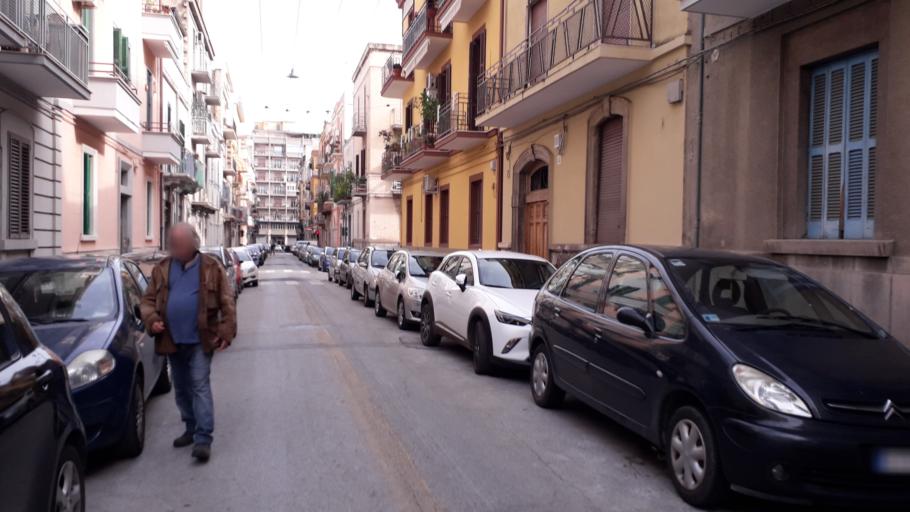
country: IT
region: Apulia
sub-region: Provincia di Bari
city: Bari
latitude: 41.1139
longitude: 16.8772
